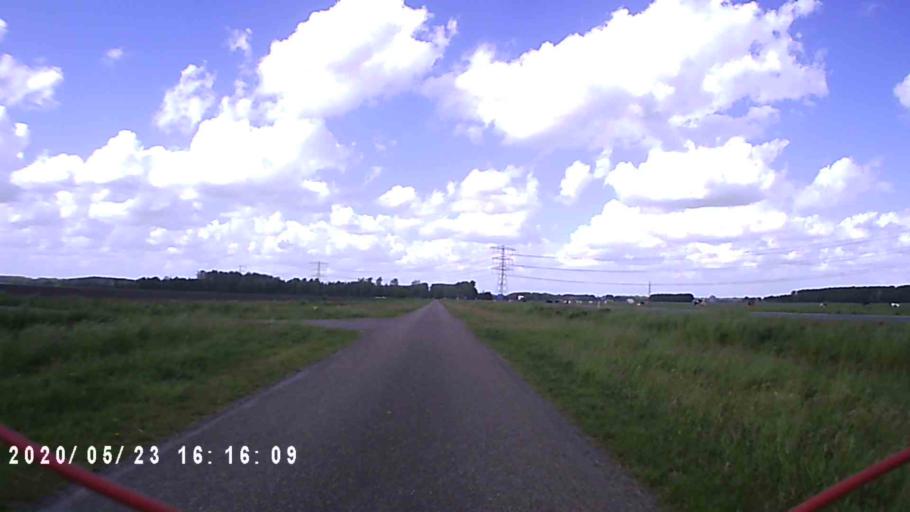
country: NL
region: Groningen
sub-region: Gemeente Appingedam
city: Appingedam
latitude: 53.2609
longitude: 6.8752
